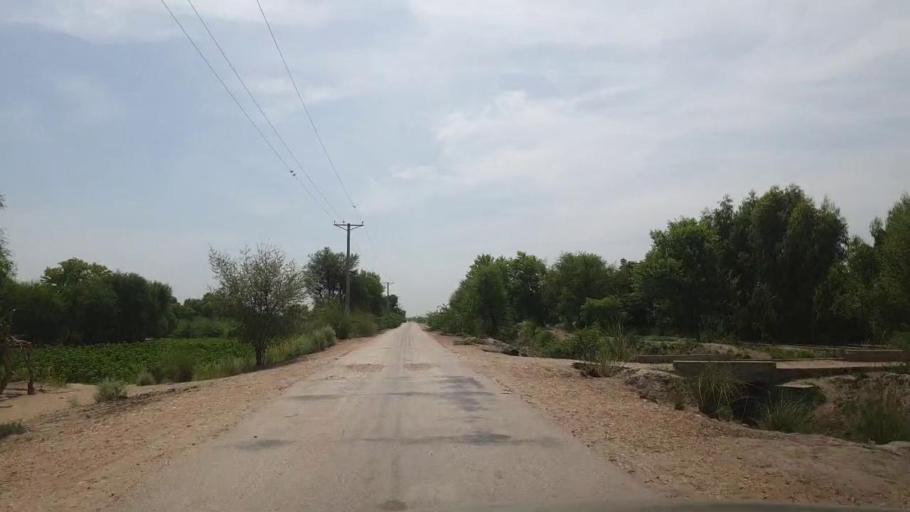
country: PK
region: Sindh
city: Kot Diji
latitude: 27.1188
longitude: 69.0056
